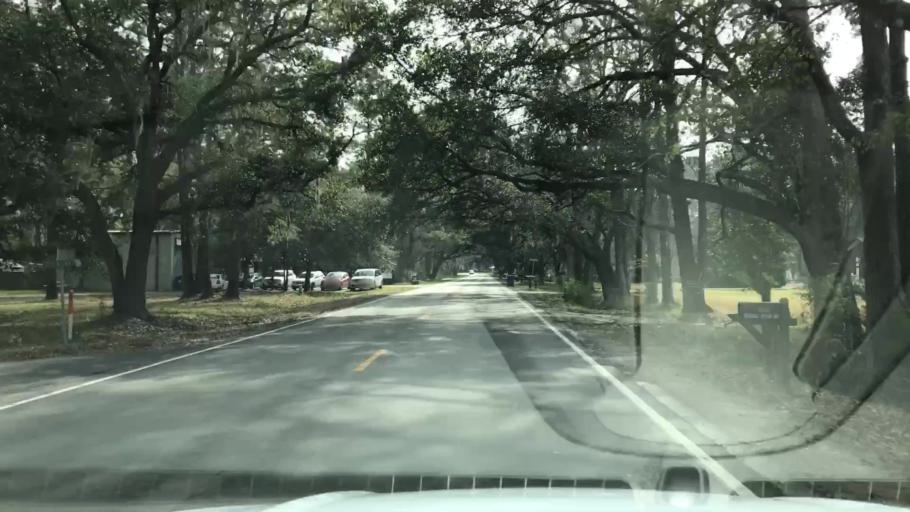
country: US
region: South Carolina
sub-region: Charleston County
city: Shell Point
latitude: 32.7354
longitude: -80.0322
